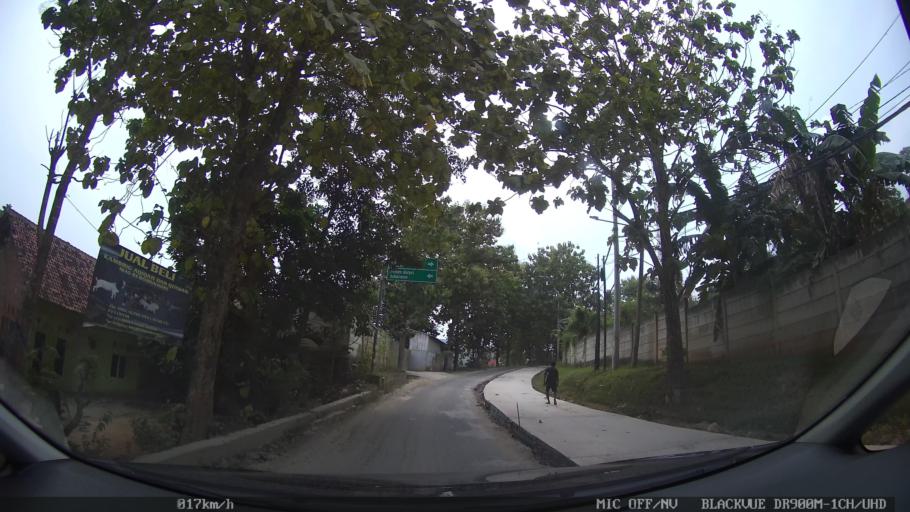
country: ID
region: Lampung
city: Bandarlampung
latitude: -5.4067
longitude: 105.3165
